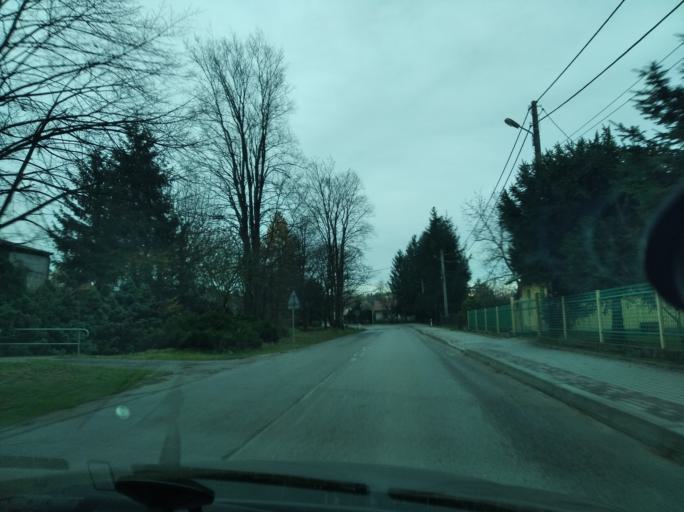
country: PL
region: Subcarpathian Voivodeship
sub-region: Powiat lancucki
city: Krzemienica
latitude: 50.0804
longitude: 22.1896
